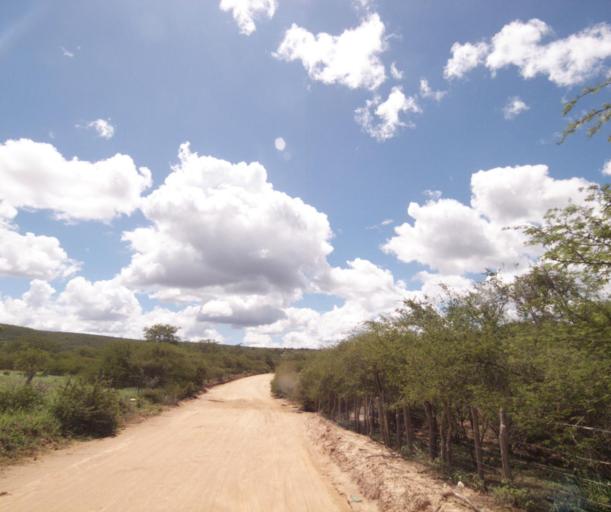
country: BR
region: Bahia
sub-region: Pocoes
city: Pocoes
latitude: -14.3799
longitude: -40.5619
